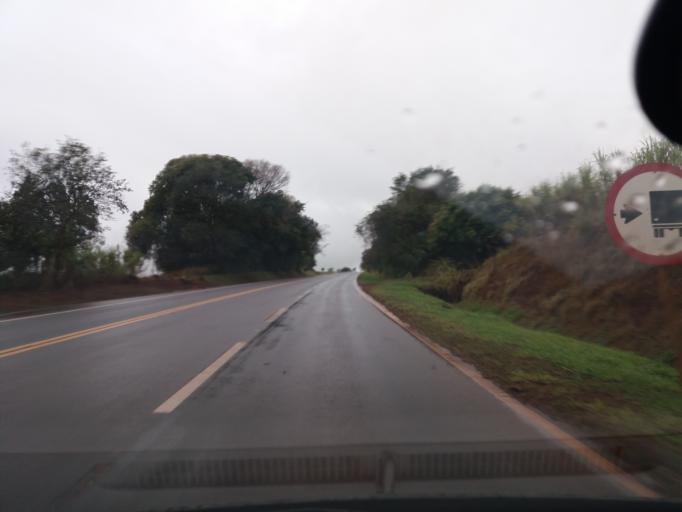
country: BR
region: Parana
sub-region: Campo Mourao
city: Campo Mourao
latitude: -24.3197
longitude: -52.6380
